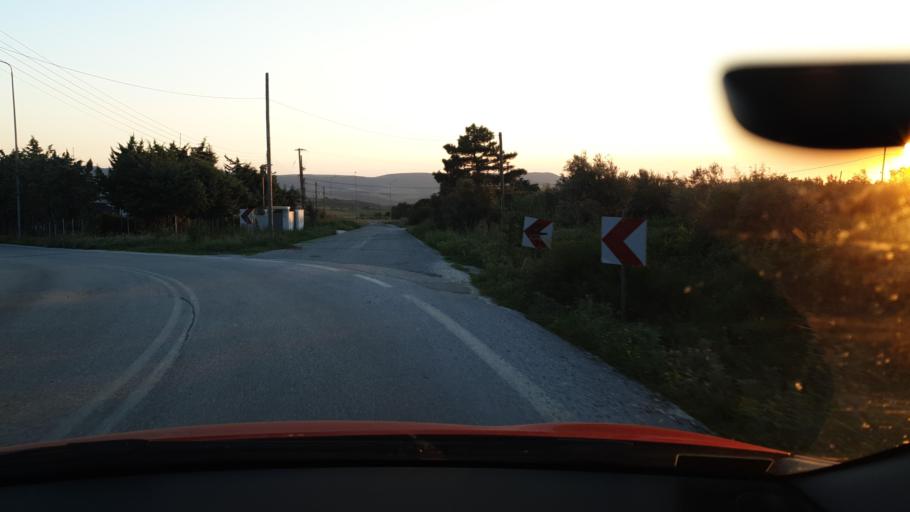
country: GR
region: Central Macedonia
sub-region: Nomos Chalkidikis
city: Galatista
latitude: 40.4683
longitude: 23.2498
